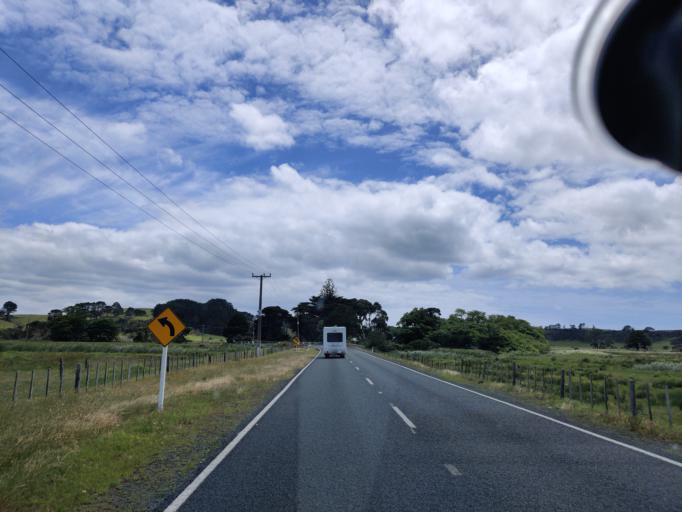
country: NZ
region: Northland
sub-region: Far North District
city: Kaitaia
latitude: -34.7614
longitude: 173.0763
